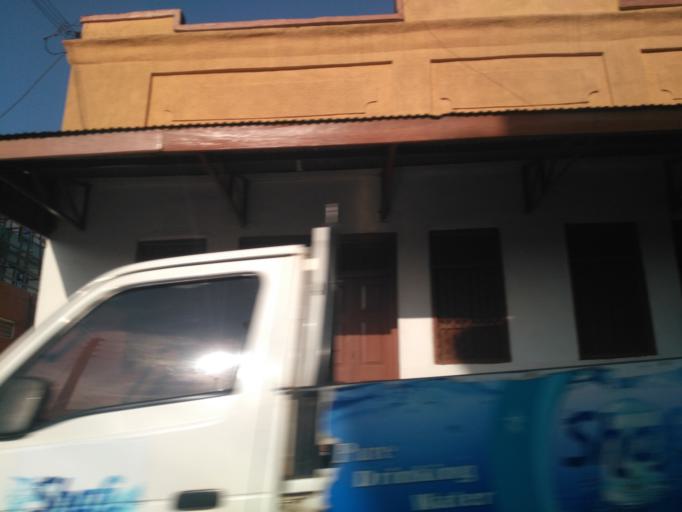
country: TZ
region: Arusha
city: Arusha
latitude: -3.3735
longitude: 36.6847
